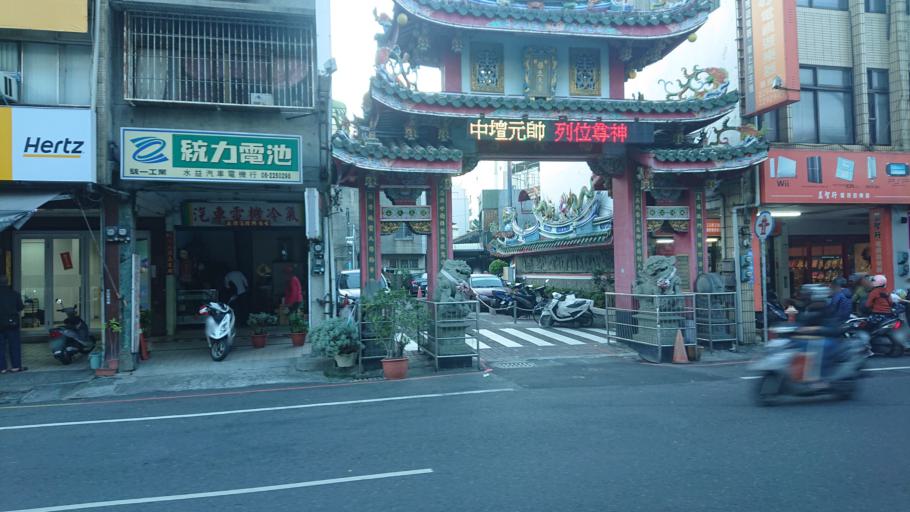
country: TW
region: Taiwan
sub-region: Tainan
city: Tainan
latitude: 22.9995
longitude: 120.2126
